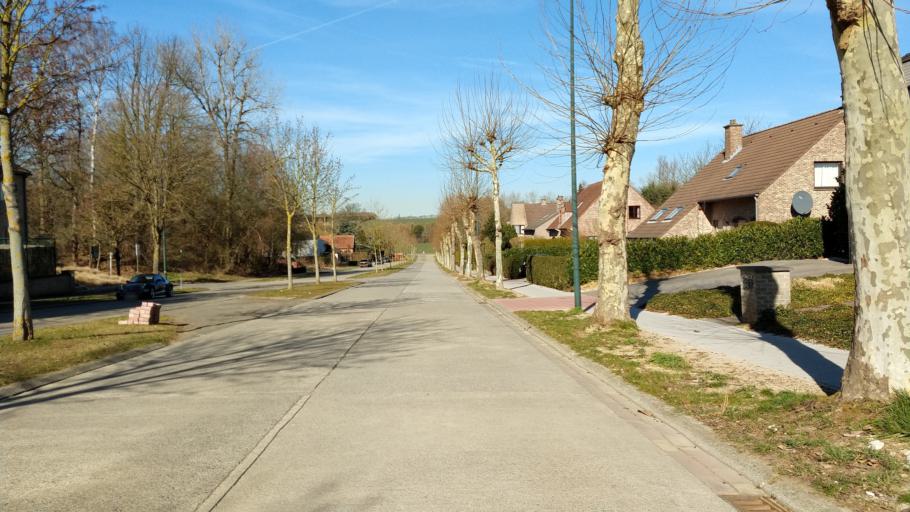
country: BE
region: Flanders
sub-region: Provincie Vlaams-Brabant
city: Wezembeek-Oppem
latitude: 50.8606
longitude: 4.4933
